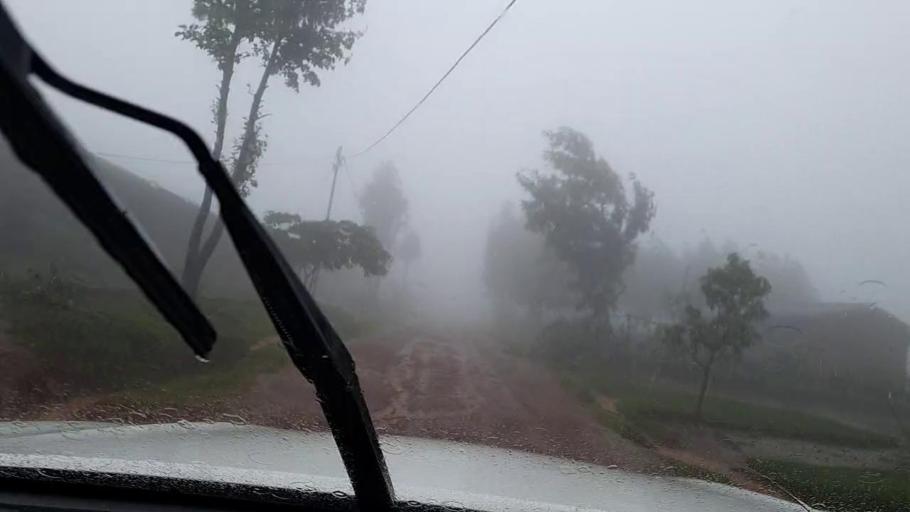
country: RW
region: Northern Province
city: Byumba
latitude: -1.7341
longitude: 30.0267
